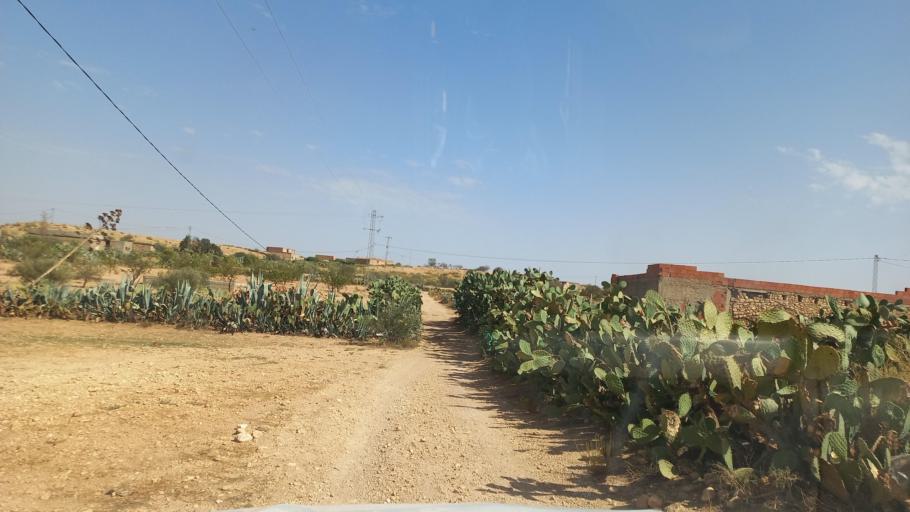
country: TN
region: Al Qasrayn
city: Kasserine
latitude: 35.2782
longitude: 8.9687
